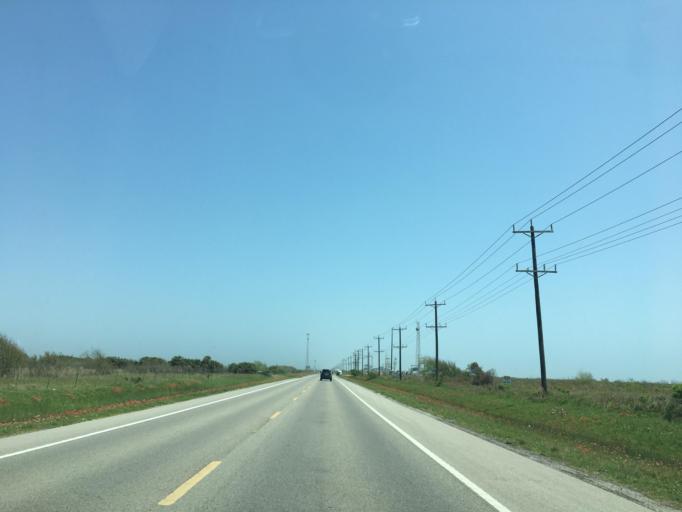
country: US
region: Texas
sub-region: Galveston County
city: Bolivar Peninsula
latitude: 29.4872
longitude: -94.5582
